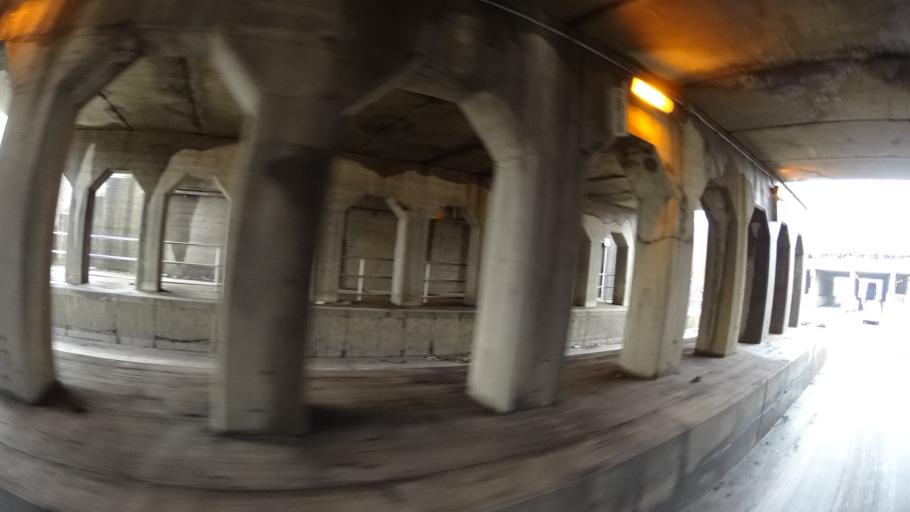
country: US
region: Illinois
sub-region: Cook County
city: East Hazel Crest
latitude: 41.5791
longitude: -87.6584
